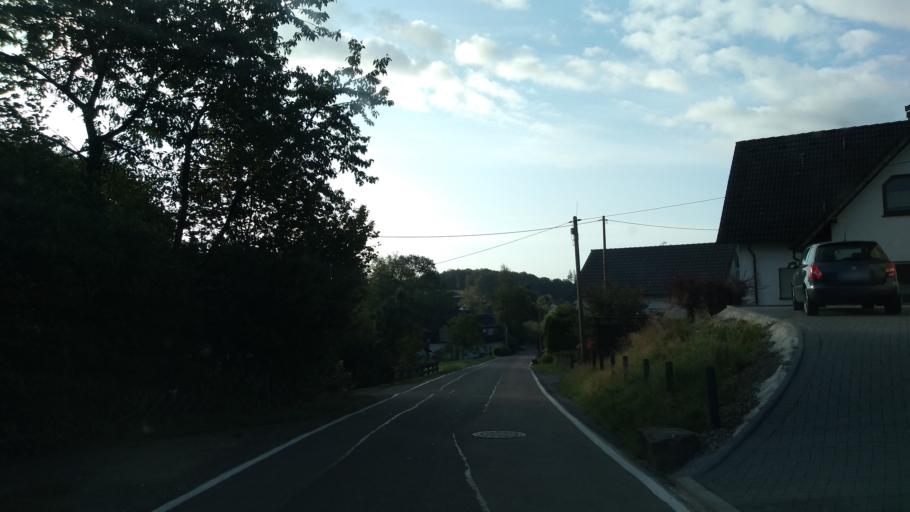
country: DE
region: North Rhine-Westphalia
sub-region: Regierungsbezirk Koln
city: Gummersbach
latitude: 51.0385
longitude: 7.5257
